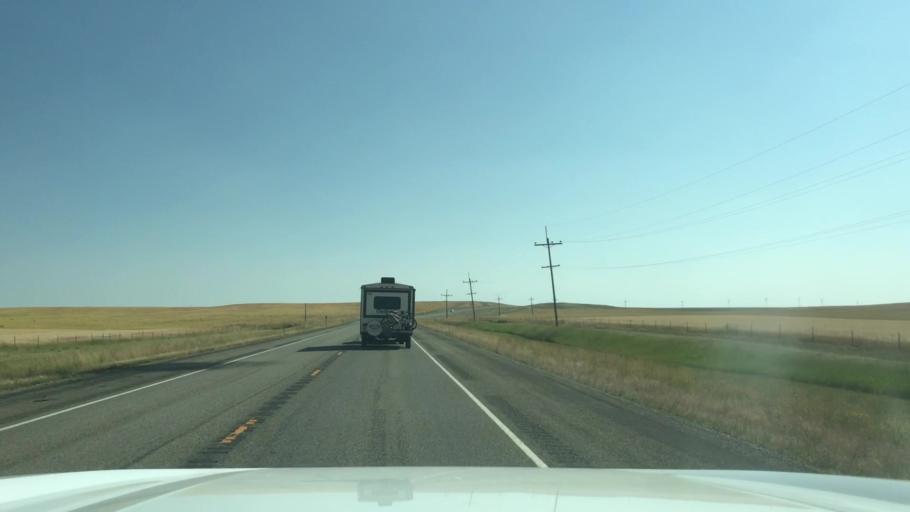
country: US
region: Montana
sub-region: Wheatland County
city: Harlowton
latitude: 46.4769
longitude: -109.7661
